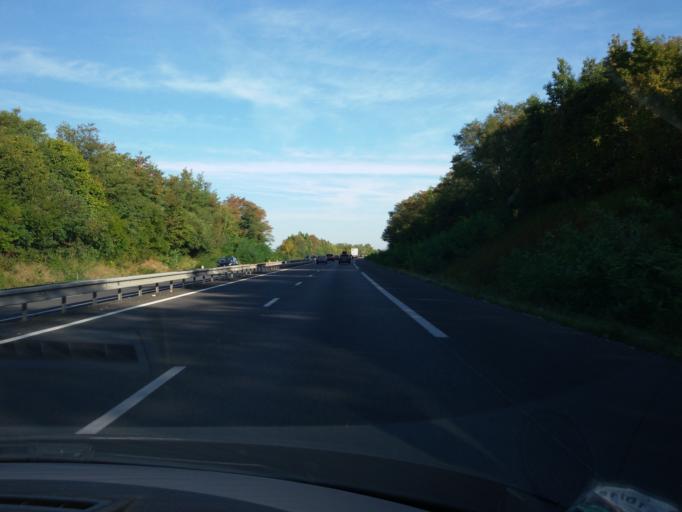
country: FR
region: Centre
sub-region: Departement du Cher
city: Mehun-sur-Yevre
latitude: 47.1142
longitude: 2.1996
